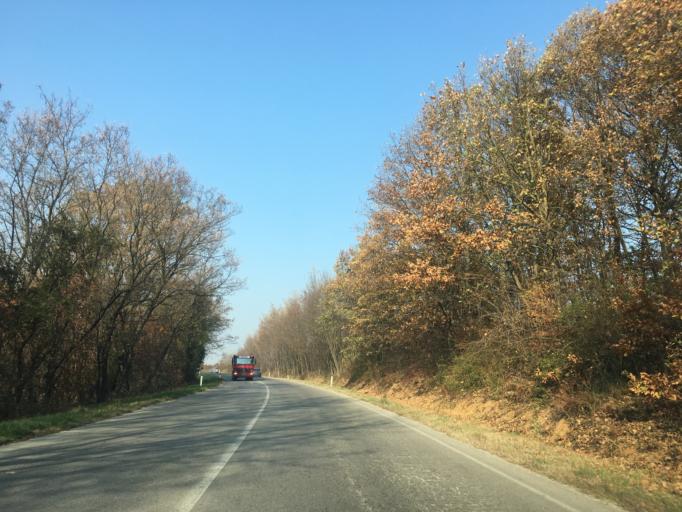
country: XK
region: Pec
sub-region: Komuna e Pejes
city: Dubova (Driloni)
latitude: 42.6465
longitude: 20.4117
